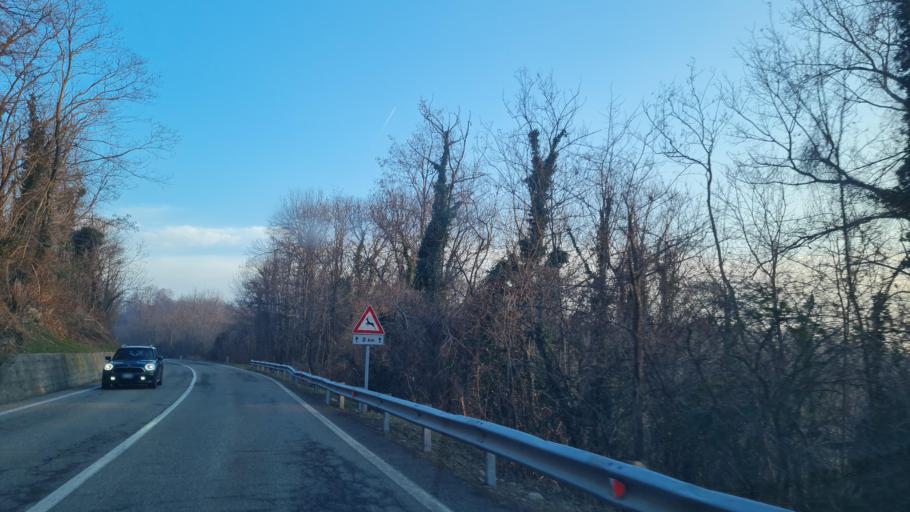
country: IT
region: Piedmont
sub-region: Provincia di Torino
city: Andrate
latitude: 45.5174
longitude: 7.8840
